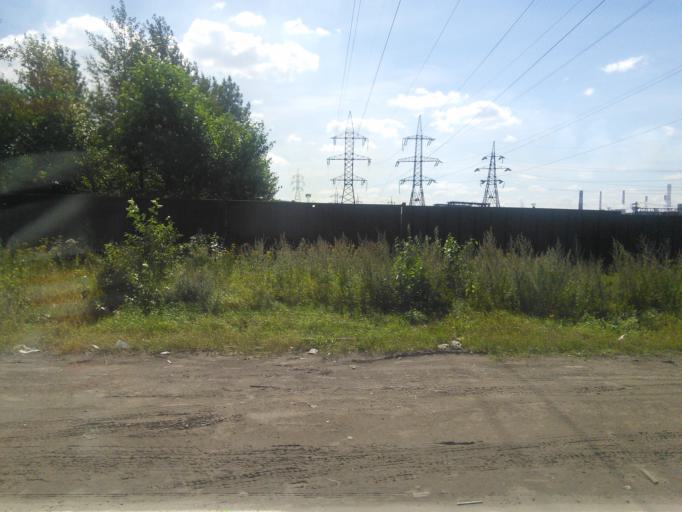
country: RU
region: Vologda
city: Cherepovets
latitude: 59.1537
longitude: 37.8651
